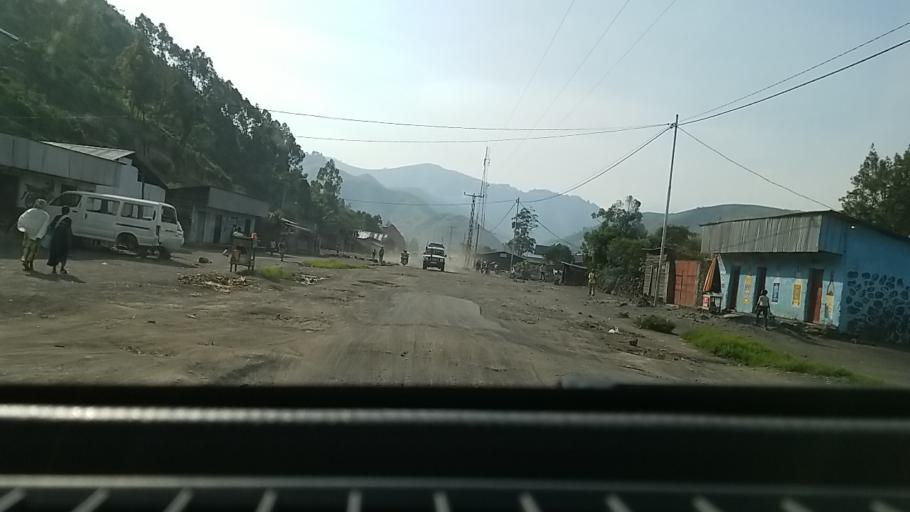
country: CD
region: Nord Kivu
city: Sake
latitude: -1.5721
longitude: 29.0572
